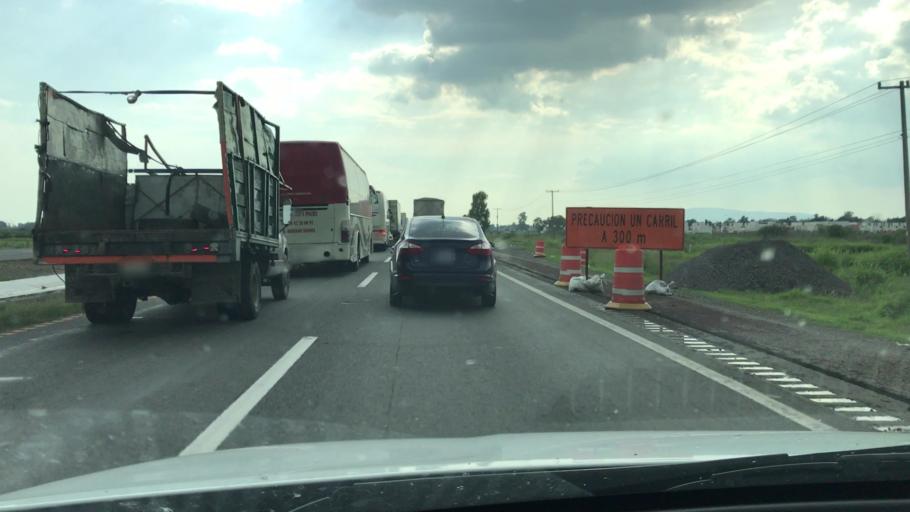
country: MX
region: Guanajuato
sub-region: Irapuato
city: Cuarta Brigada
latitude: 20.6536
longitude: -101.3052
